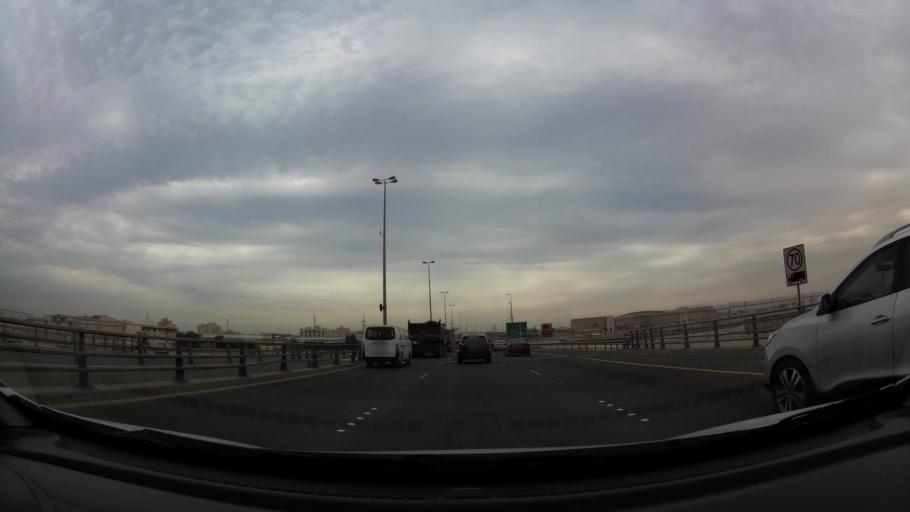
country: BH
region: Northern
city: Sitrah
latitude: 26.1743
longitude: 50.5979
